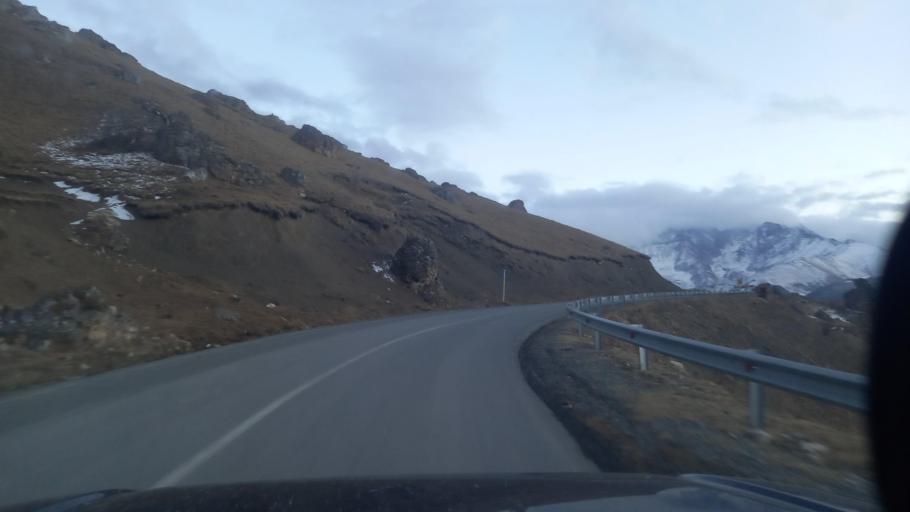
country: RU
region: Ingushetiya
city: Dzhayrakh
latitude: 42.8218
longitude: 44.8302
